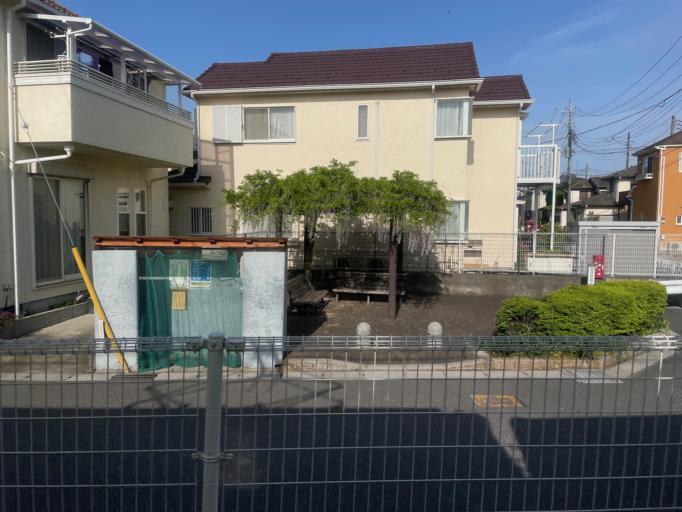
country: JP
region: Chiba
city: Nagareyama
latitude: 35.8496
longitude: 139.9013
